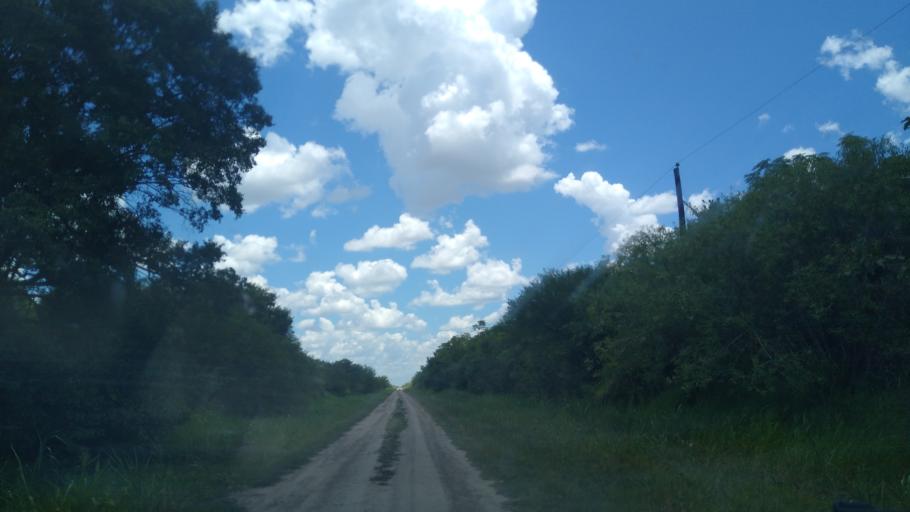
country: AR
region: Chaco
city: Presidencia Roque Saenz Pena
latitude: -26.7476
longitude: -60.3383
